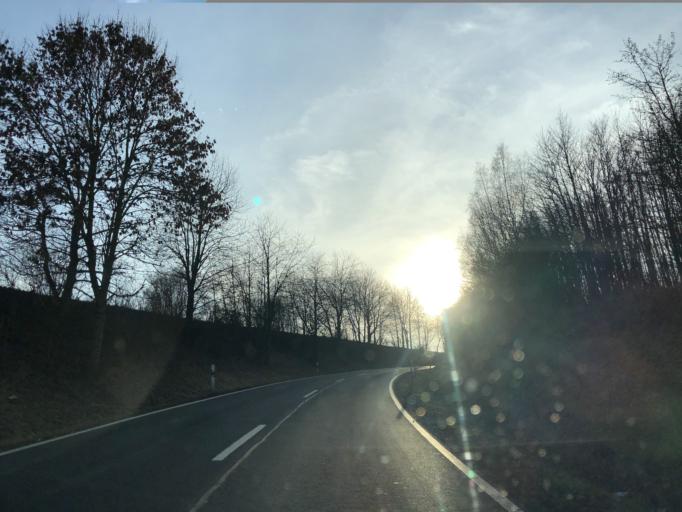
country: DE
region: Bavaria
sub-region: Regierungsbezirk Unterfranken
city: Reichenberg
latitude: 49.7178
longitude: 9.9537
